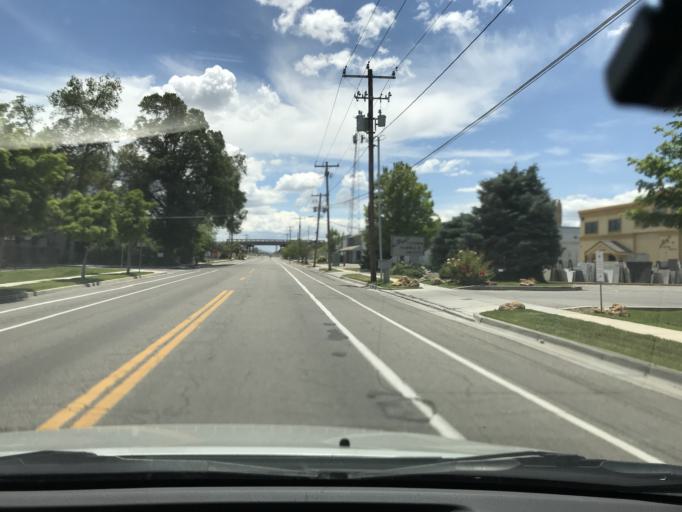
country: US
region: Utah
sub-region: Salt Lake County
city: Centerfield
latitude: 40.6901
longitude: -111.8998
